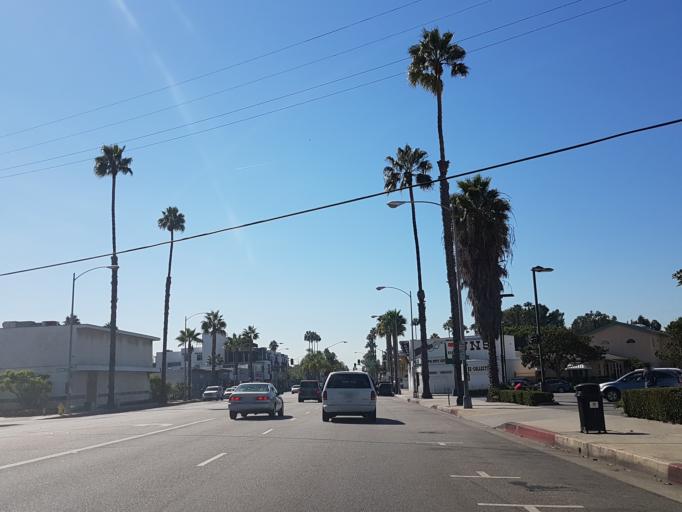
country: US
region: California
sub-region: Los Angeles County
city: Culver City
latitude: 34.0118
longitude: -118.4105
